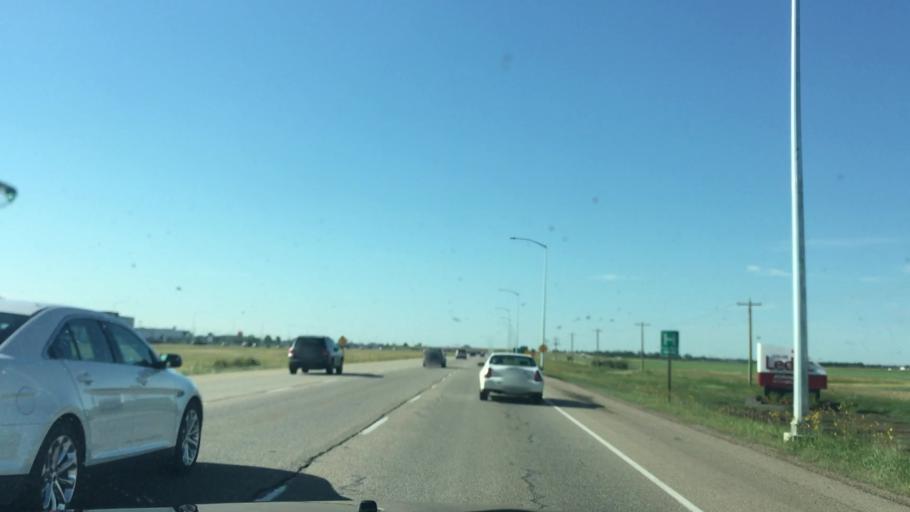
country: CA
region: Alberta
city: Leduc
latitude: 53.2963
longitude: -113.5499
